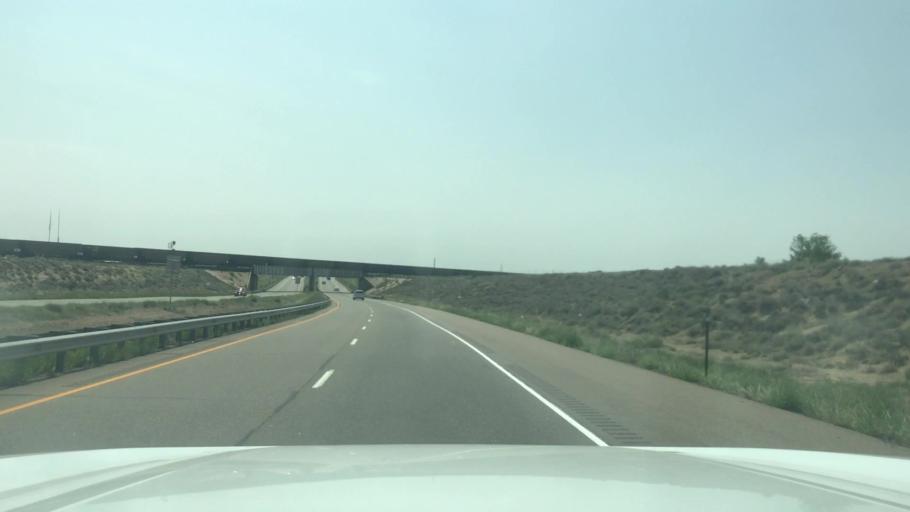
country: US
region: Colorado
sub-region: Pueblo County
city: Pueblo West
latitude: 38.3910
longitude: -104.6201
